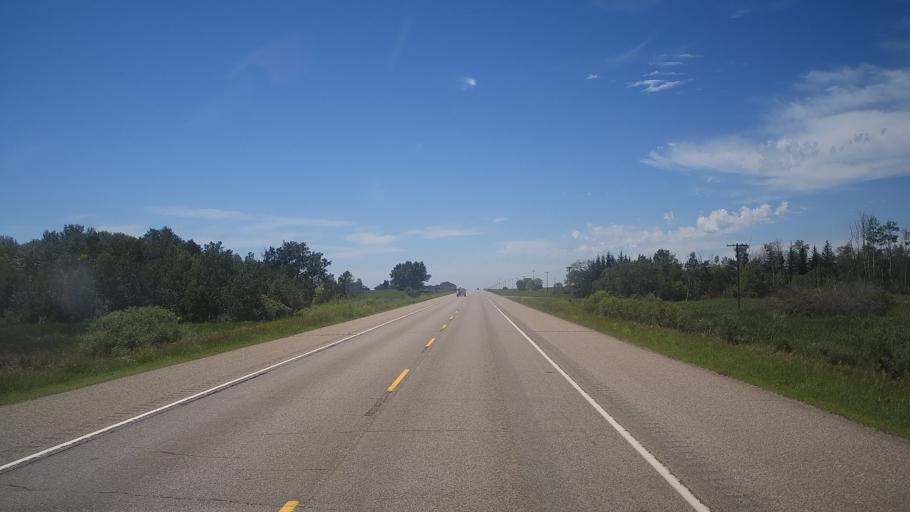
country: CA
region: Saskatchewan
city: Langenburg
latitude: 50.7714
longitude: -101.3078
